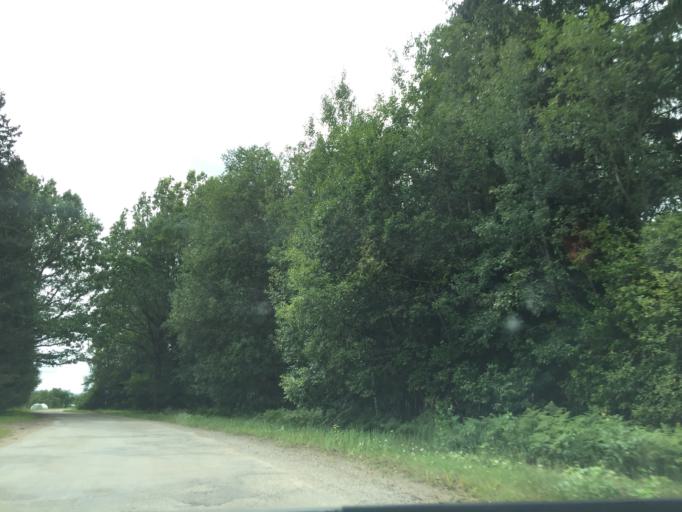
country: LV
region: Ogre
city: Jumprava
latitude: 56.7737
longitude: 24.9491
